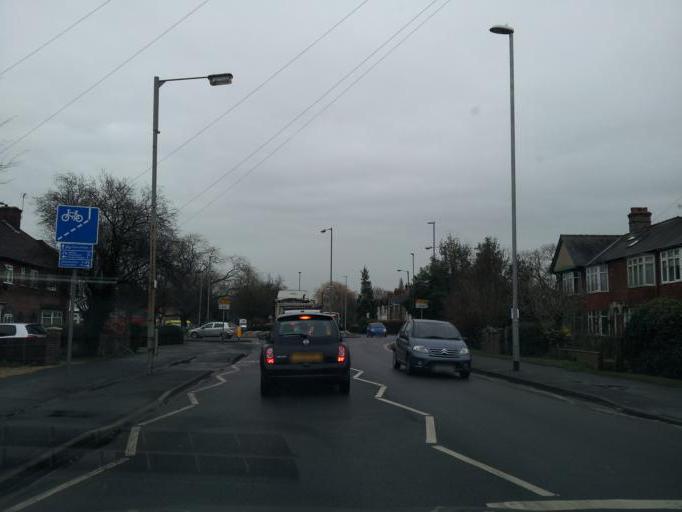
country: GB
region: England
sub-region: Cambridgeshire
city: Cambridge
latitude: 52.1869
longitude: 0.1518
